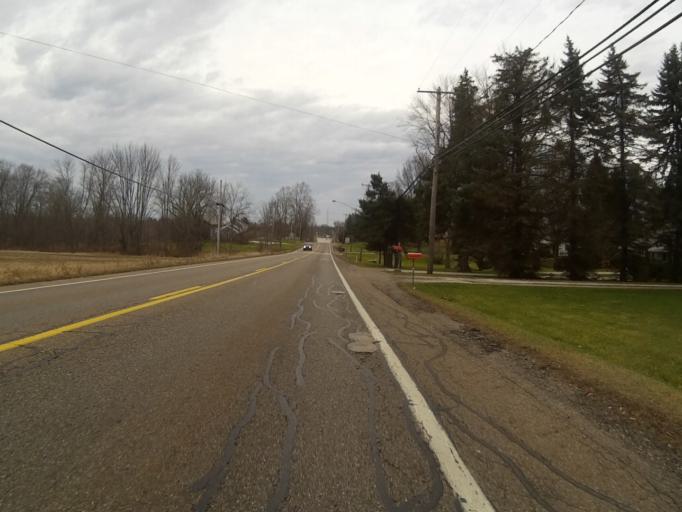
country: US
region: Ohio
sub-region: Portage County
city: Brimfield
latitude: 41.0926
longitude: -81.3464
